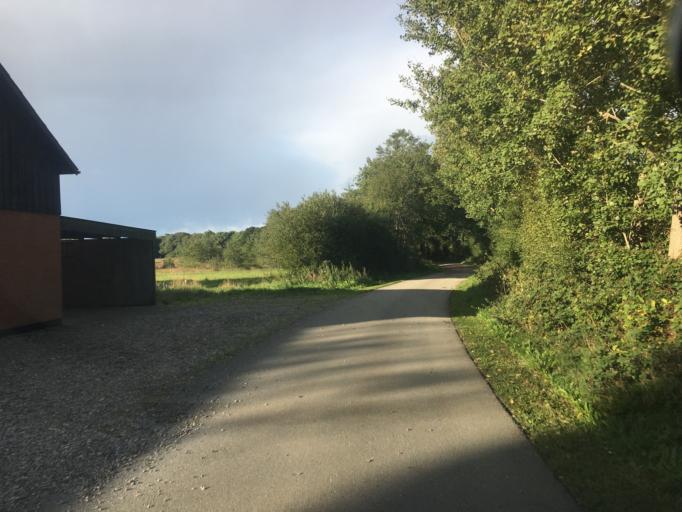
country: DK
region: South Denmark
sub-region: Tonder Kommune
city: Logumkloster
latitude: 55.0211
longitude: 8.9642
